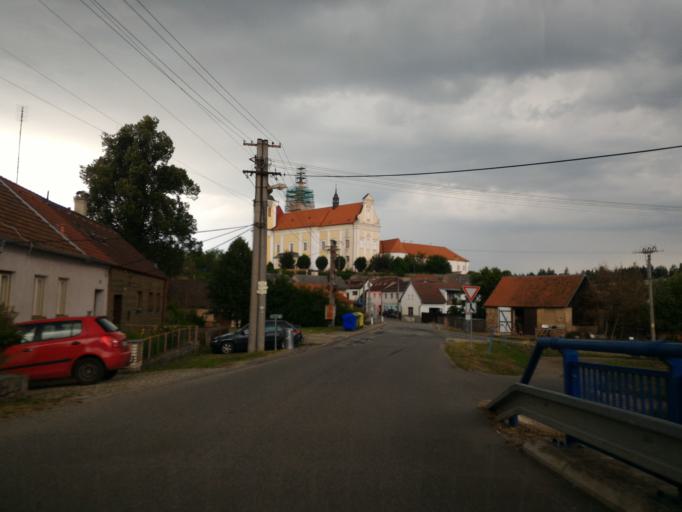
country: CZ
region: Vysocina
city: Zeletava
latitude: 49.1372
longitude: 15.5662
